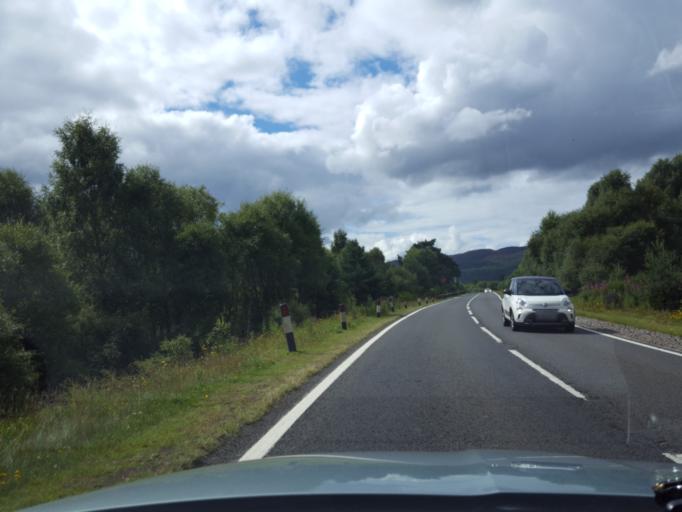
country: GB
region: Scotland
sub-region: Highland
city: Aviemore
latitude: 57.2178
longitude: -3.8152
